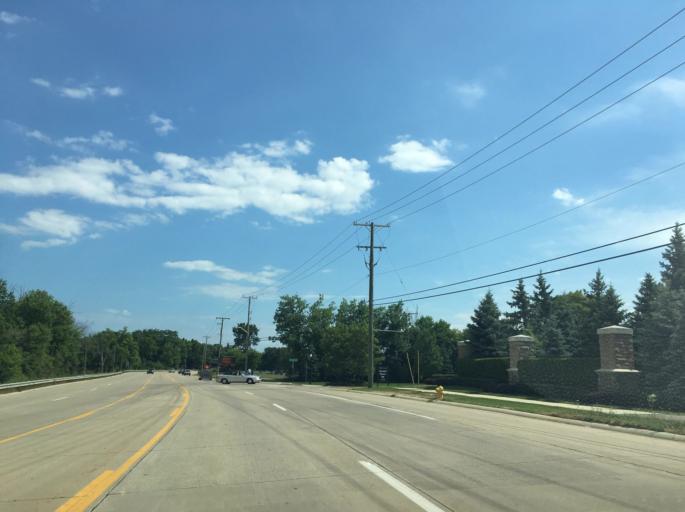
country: US
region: Michigan
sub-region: Macomb County
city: Clinton
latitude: 42.6194
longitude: -82.9345
